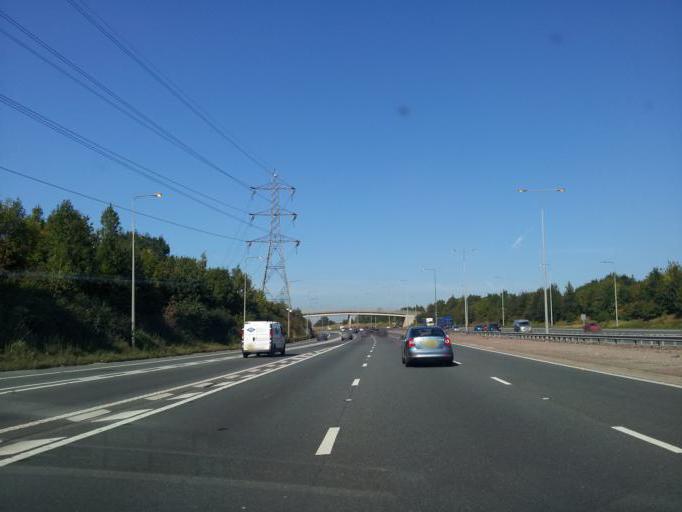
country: GB
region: England
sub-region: Borough of Rochdale
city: Middleton
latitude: 53.5362
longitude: -2.2097
